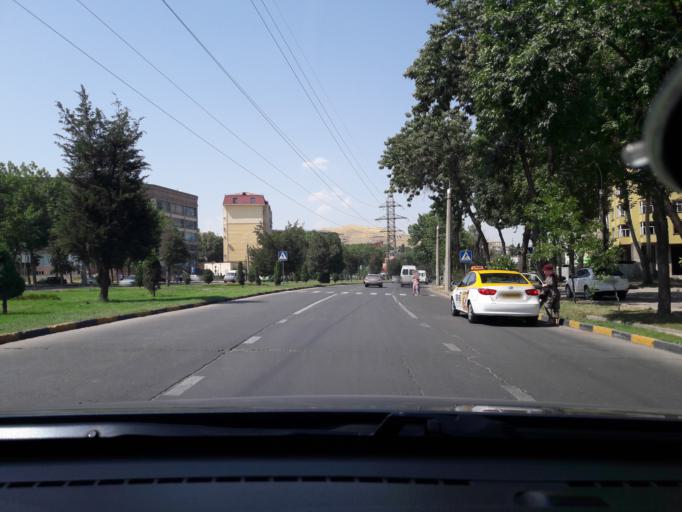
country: TJ
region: Dushanbe
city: Dushanbe
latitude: 38.5883
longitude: 68.7413
